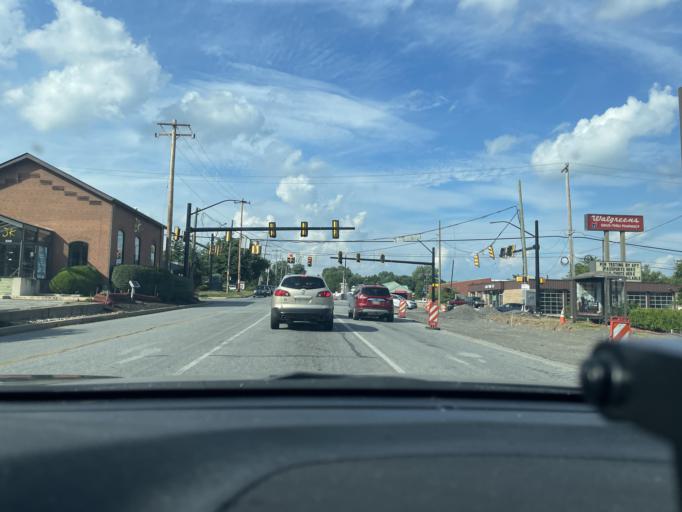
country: US
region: Pennsylvania
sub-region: Montgomery County
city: Norristown
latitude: 40.1482
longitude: -75.3079
